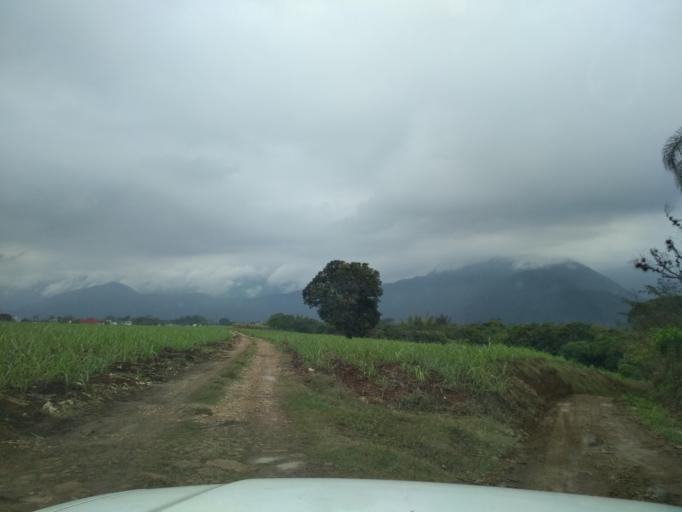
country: MX
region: Veracruz
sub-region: Cordoba
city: San Jose de Tapia
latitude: 18.8500
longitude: -96.9701
